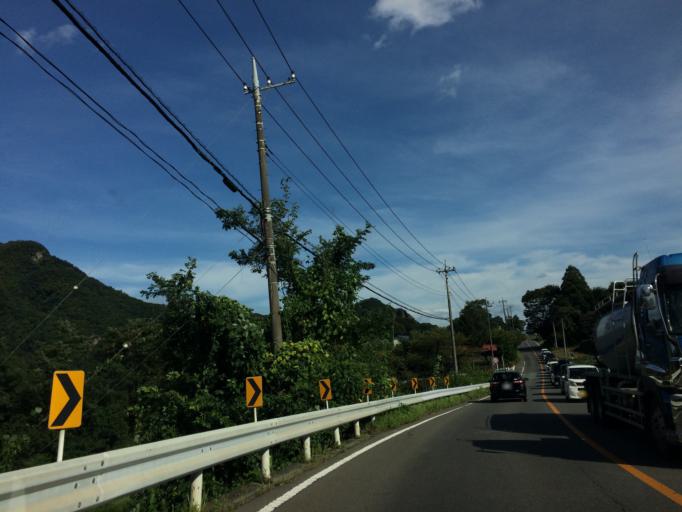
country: JP
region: Gunma
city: Nakanojomachi
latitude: 36.5653
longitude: 138.8848
